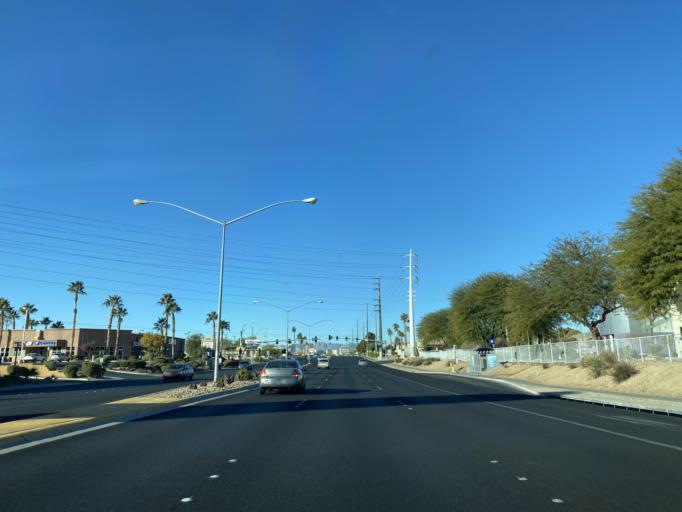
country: US
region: Nevada
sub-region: Clark County
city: Winchester
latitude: 36.1151
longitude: -115.1079
